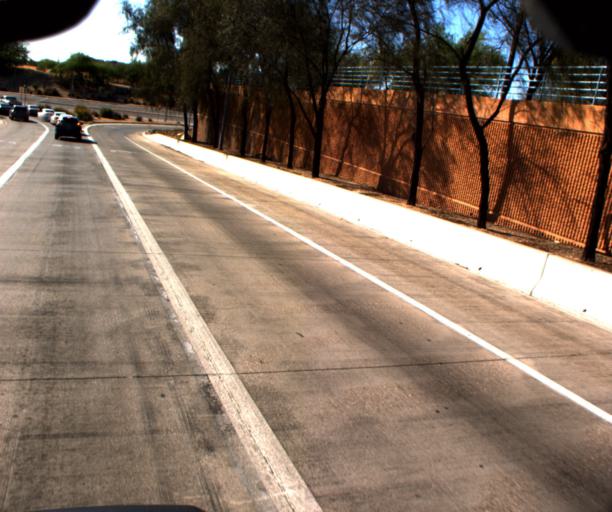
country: US
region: Arizona
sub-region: Pima County
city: South Tucson
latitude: 32.2201
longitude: -110.9608
